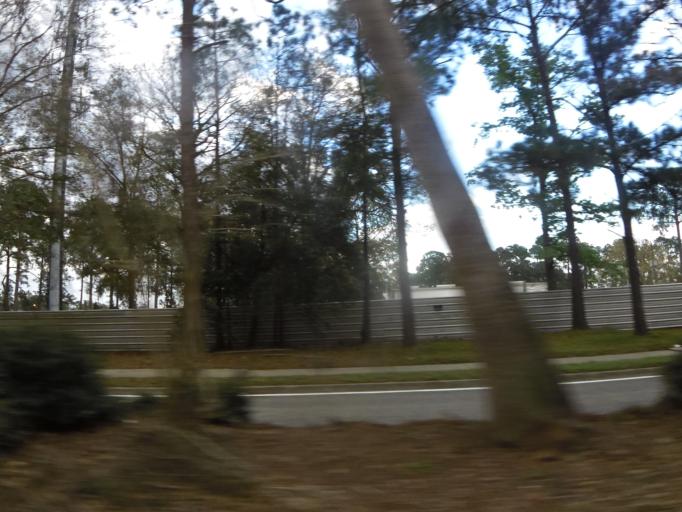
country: US
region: Florida
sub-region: Saint Johns County
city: Fruit Cove
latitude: 30.2075
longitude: -81.5835
